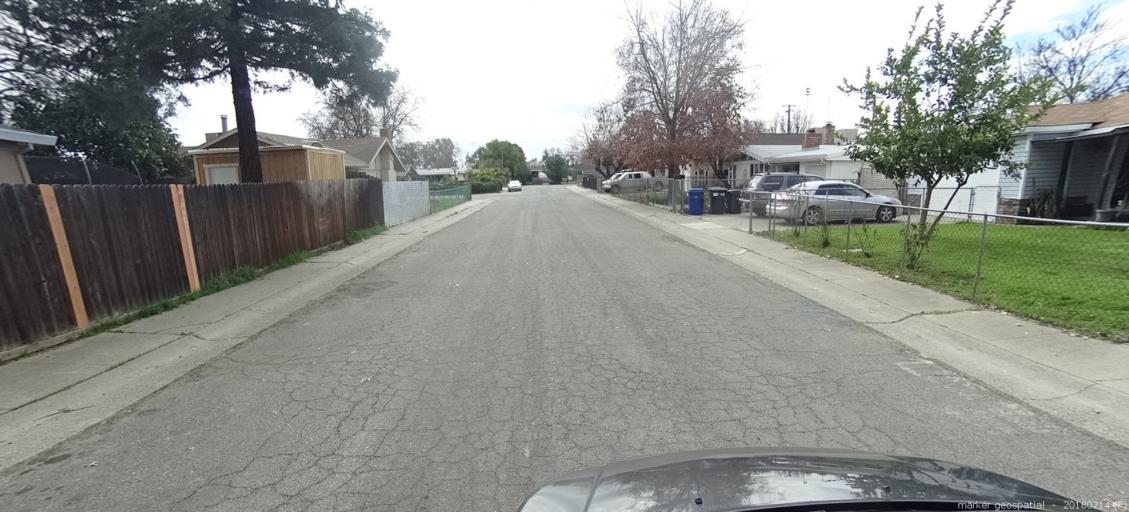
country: US
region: California
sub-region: Sacramento County
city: Rio Linda
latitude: 38.6855
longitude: -121.4634
